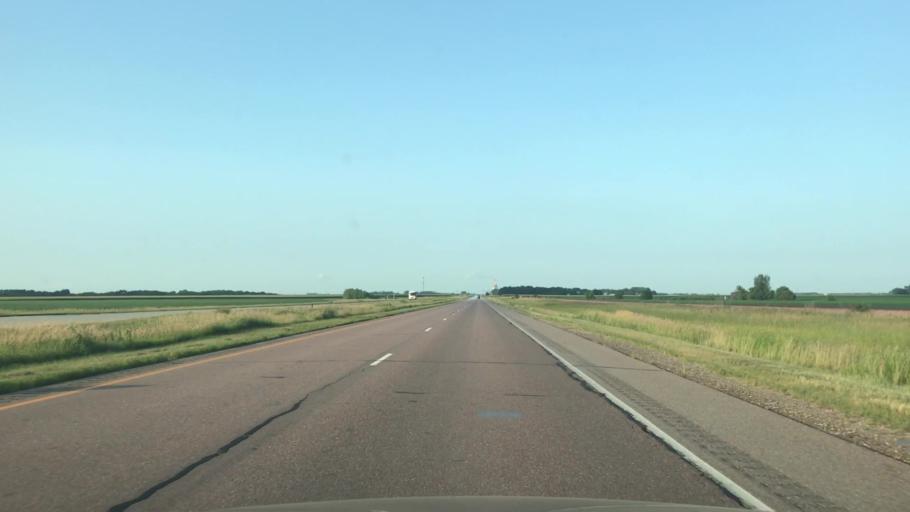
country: US
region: Minnesota
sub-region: Jackson County
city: Lakefield
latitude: 43.7477
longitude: -95.3959
